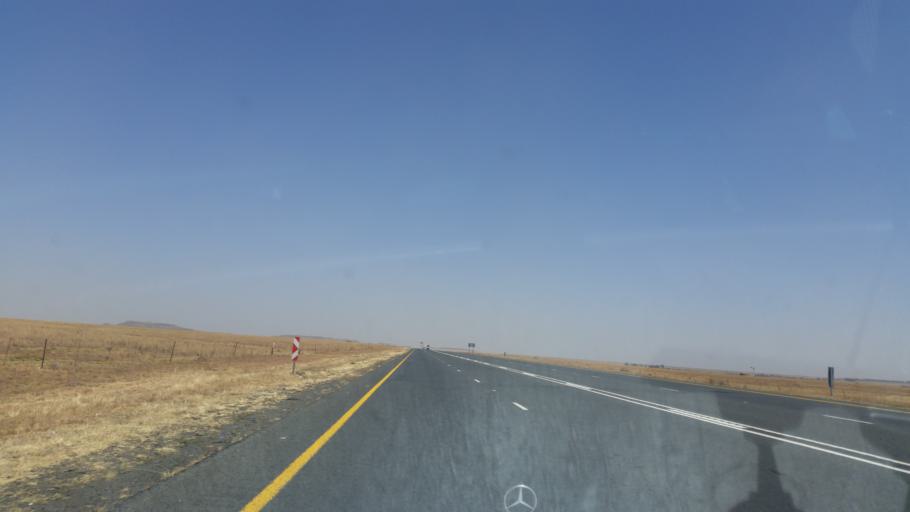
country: ZA
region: Orange Free State
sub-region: Lejweleputswa District Municipality
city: Brandfort
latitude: -28.7649
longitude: 26.7301
